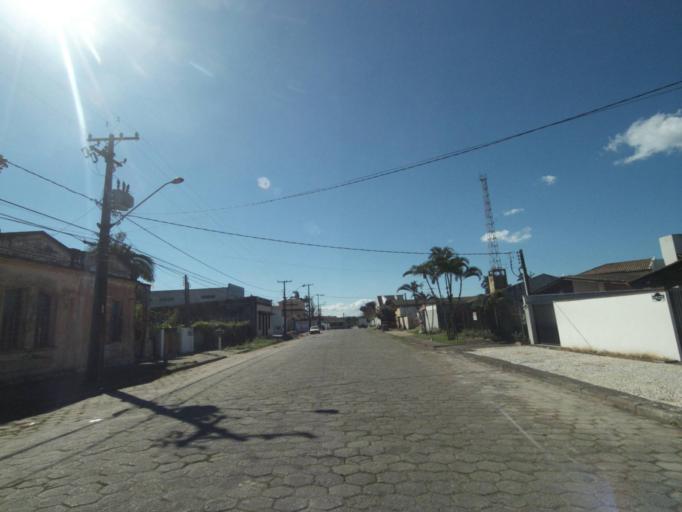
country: BR
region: Parana
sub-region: Paranagua
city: Paranagua
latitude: -25.5141
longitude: -48.5007
